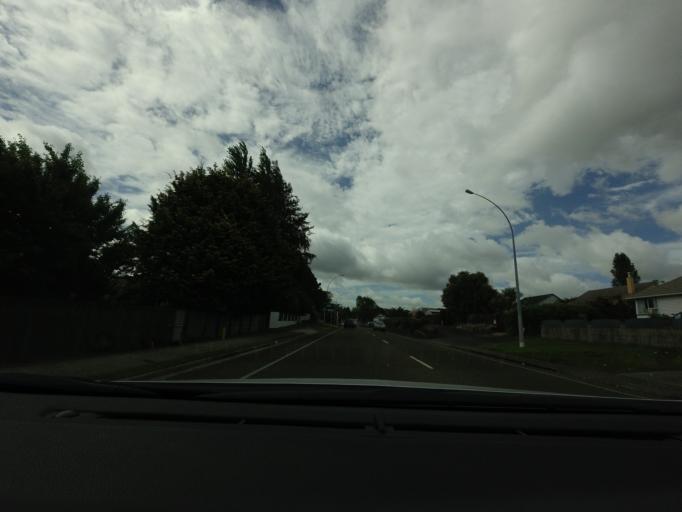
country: NZ
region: Bay of Plenty
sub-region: Rotorua District
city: Rotorua
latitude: -38.1521
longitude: 176.2400
